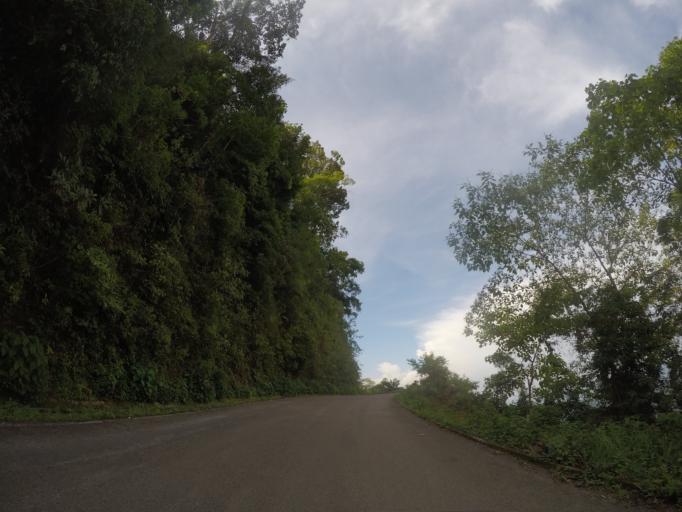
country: MX
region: Oaxaca
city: Pluma Hidalgo
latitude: 15.9371
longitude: -96.4317
